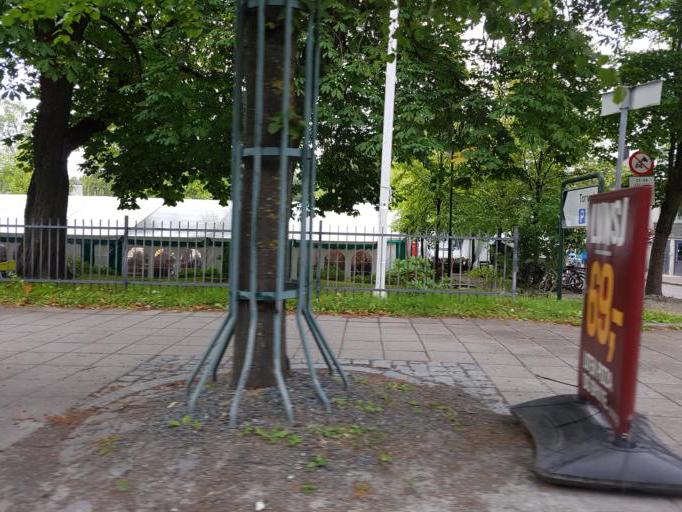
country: NO
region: Nord-Trondelag
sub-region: Levanger
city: Levanger
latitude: 63.7464
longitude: 11.2988
